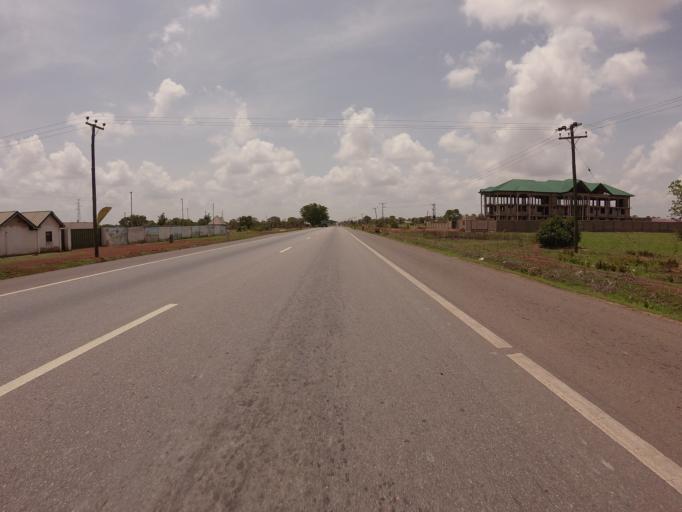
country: GH
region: Northern
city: Tamale
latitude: 9.3506
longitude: -0.9025
